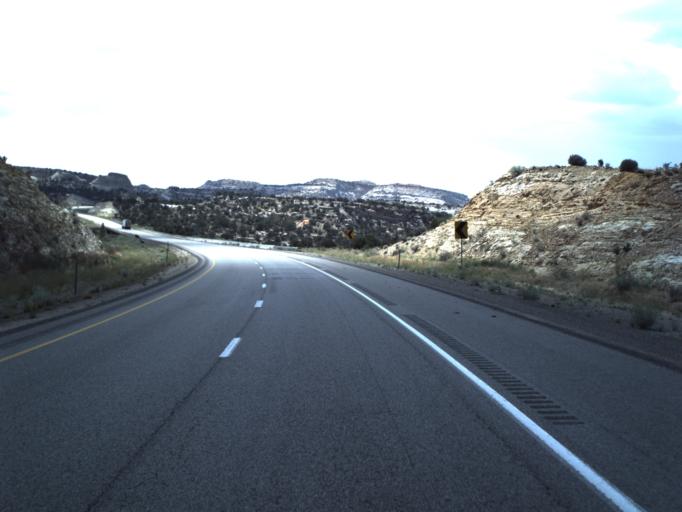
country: US
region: Utah
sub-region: Emery County
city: Ferron
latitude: 38.8625
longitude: -110.8630
